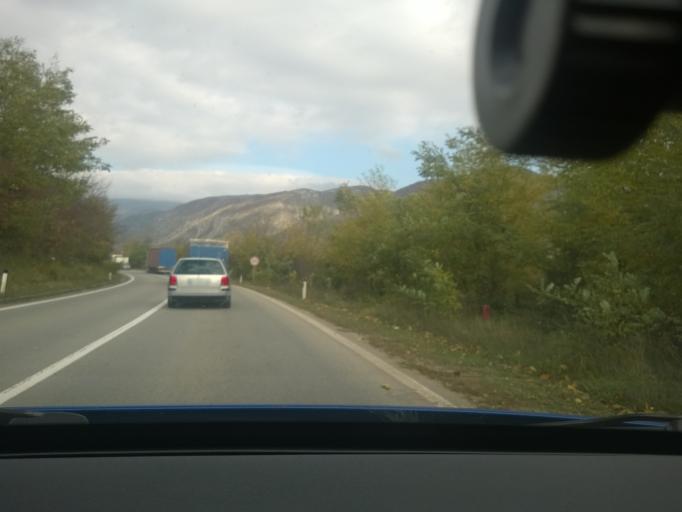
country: RS
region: Central Serbia
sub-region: Pirotski Okrug
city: Bela Palanka
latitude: 43.2867
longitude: 22.2195
